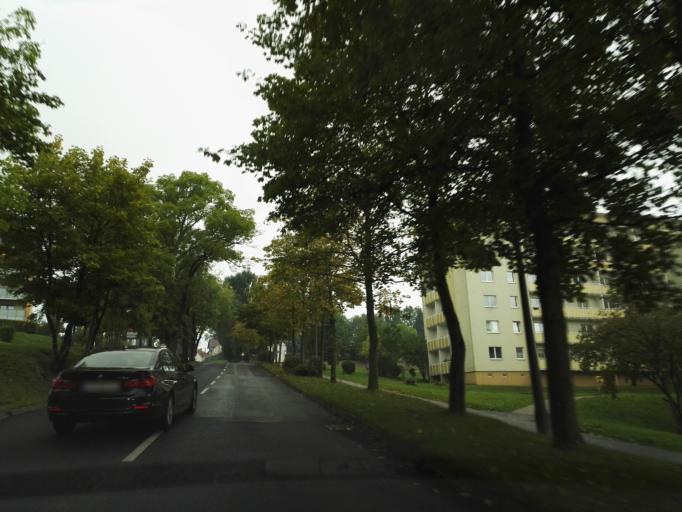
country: DE
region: Thuringia
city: Neuhaus
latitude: 50.6969
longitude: 10.9260
